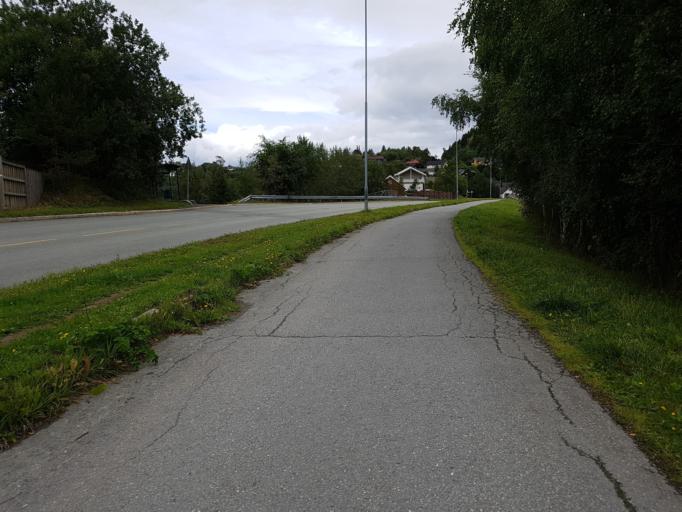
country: NO
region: Sor-Trondelag
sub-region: Trondheim
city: Trondheim
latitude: 63.3951
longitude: 10.4405
